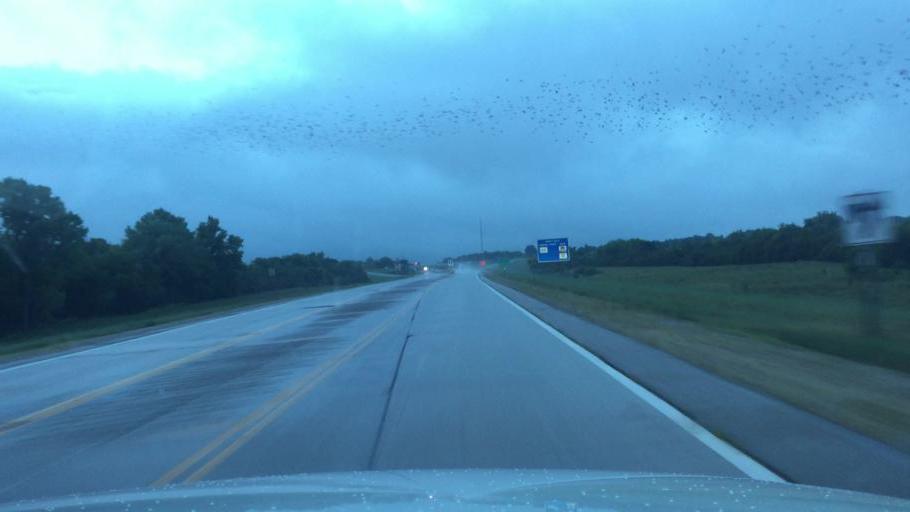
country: US
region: Kansas
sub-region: Neosho County
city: Chanute
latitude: 37.6967
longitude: -95.4795
